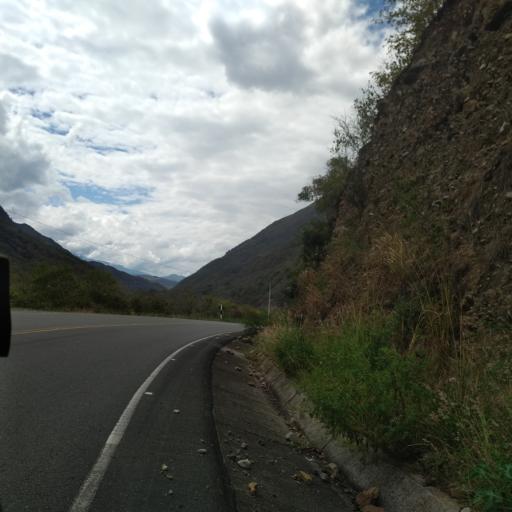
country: PE
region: Cajamarca
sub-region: Provincia de San Ignacio
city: Chirinos
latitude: -5.2355
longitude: -78.8590
